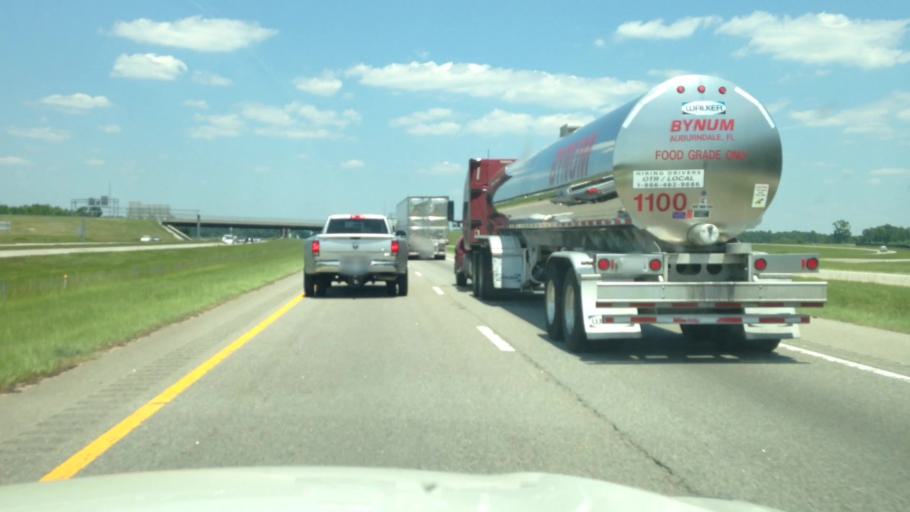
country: US
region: North Carolina
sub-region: Robeson County
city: Fairmont
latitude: 34.5905
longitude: -79.1154
